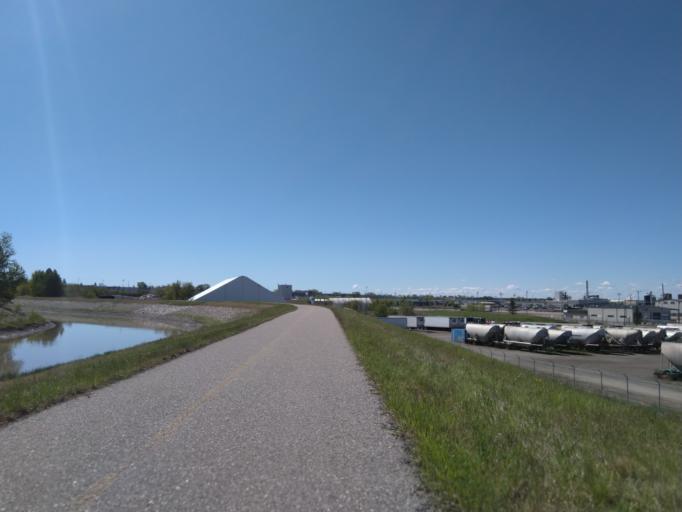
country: CA
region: Alberta
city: Calgary
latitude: 50.9970
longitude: -113.9915
